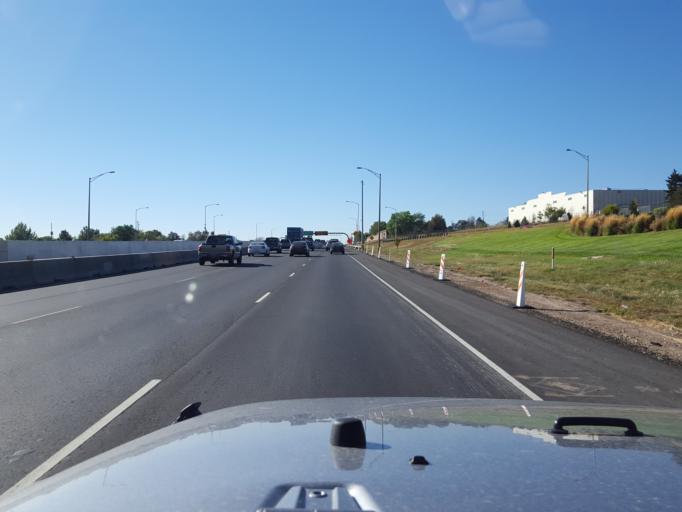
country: US
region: Colorado
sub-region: Adams County
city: Federal Heights
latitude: 39.8484
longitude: -104.9856
